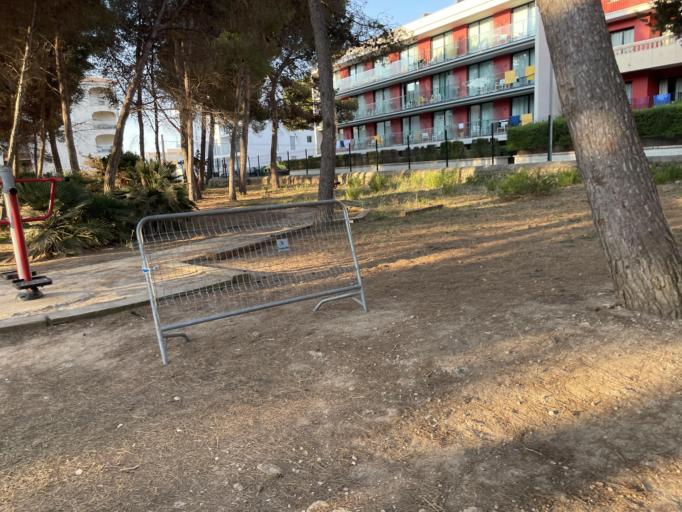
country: ES
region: Balearic Islands
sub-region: Illes Balears
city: Capdepera
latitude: 39.7166
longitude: 3.4641
